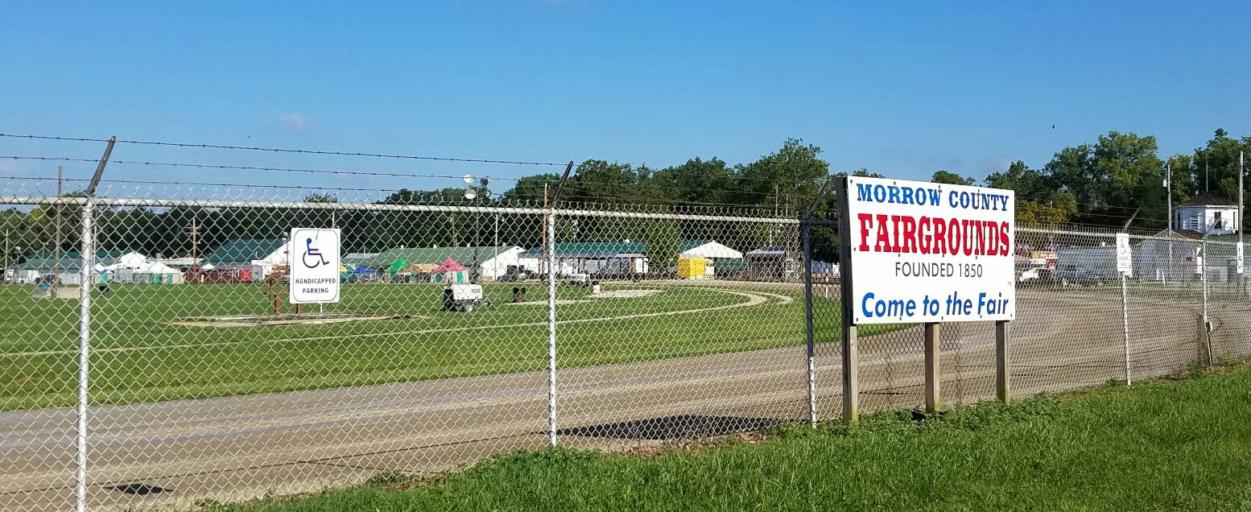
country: US
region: Ohio
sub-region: Morrow County
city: Mount Gilead
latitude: 40.5429
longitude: -82.8304
